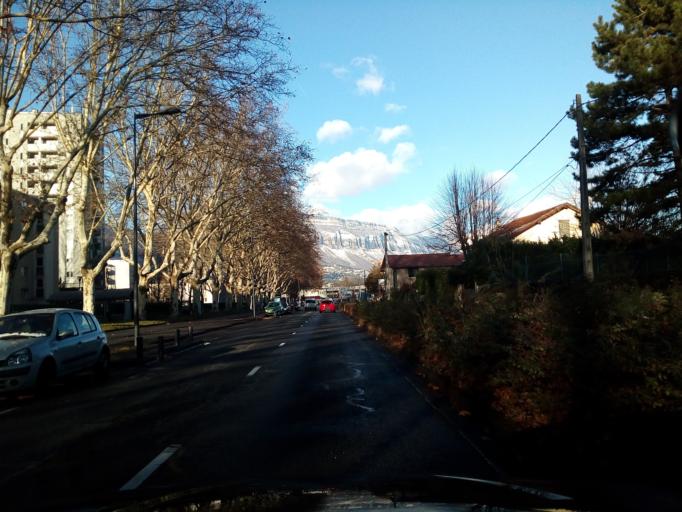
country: FR
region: Rhone-Alpes
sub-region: Departement de l'Isere
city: Saint-Martin-d'Heres
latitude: 45.1709
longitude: 5.7451
